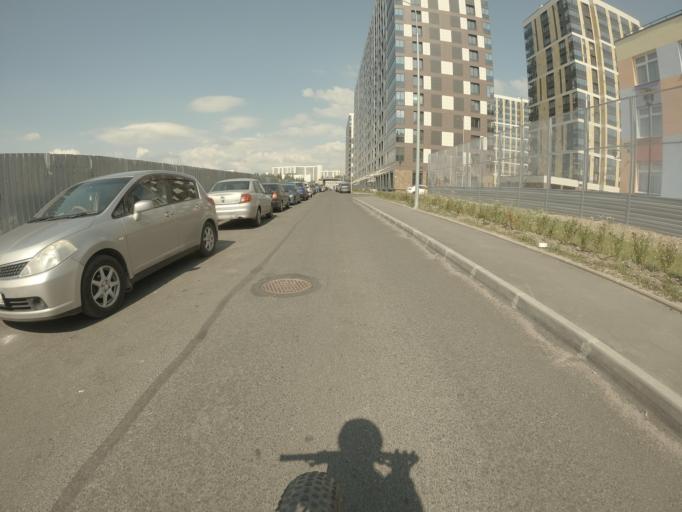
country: RU
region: St.-Petersburg
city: Obukhovo
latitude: 59.9061
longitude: 30.4394
